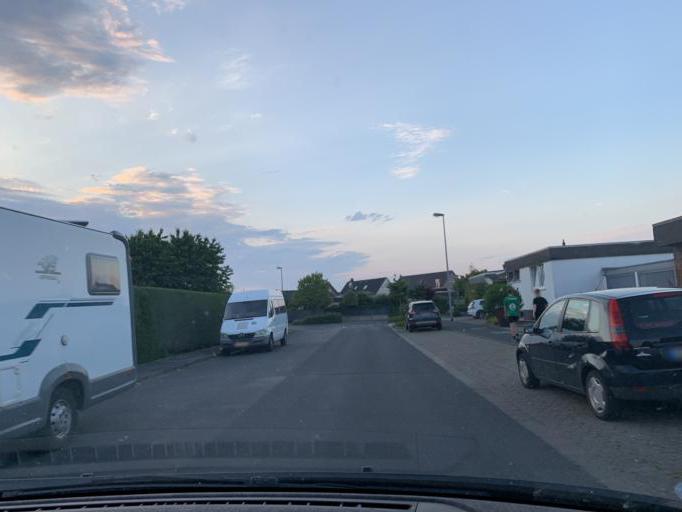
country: DE
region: North Rhine-Westphalia
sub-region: Regierungsbezirk Koln
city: Pulheim
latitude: 50.9975
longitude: 6.8185
